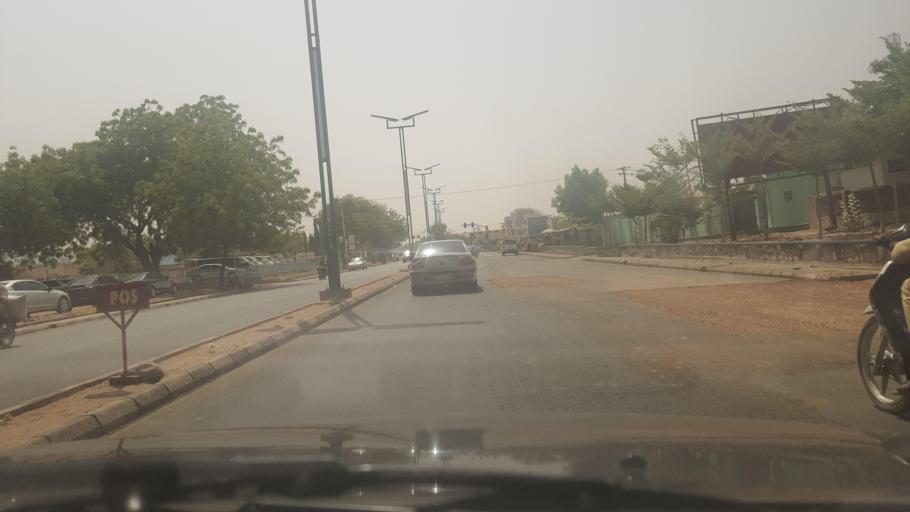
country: NG
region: Gombe
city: Gombe
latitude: 10.2858
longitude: 11.1424
